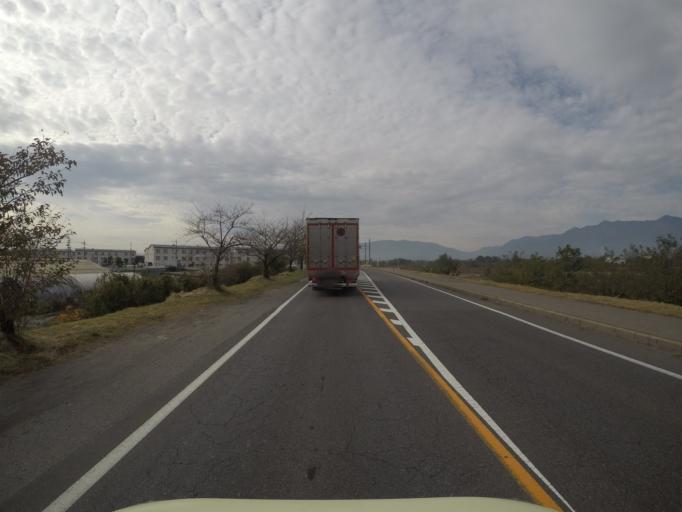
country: JP
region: Nagano
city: Matsumoto
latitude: 36.2403
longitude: 137.9153
